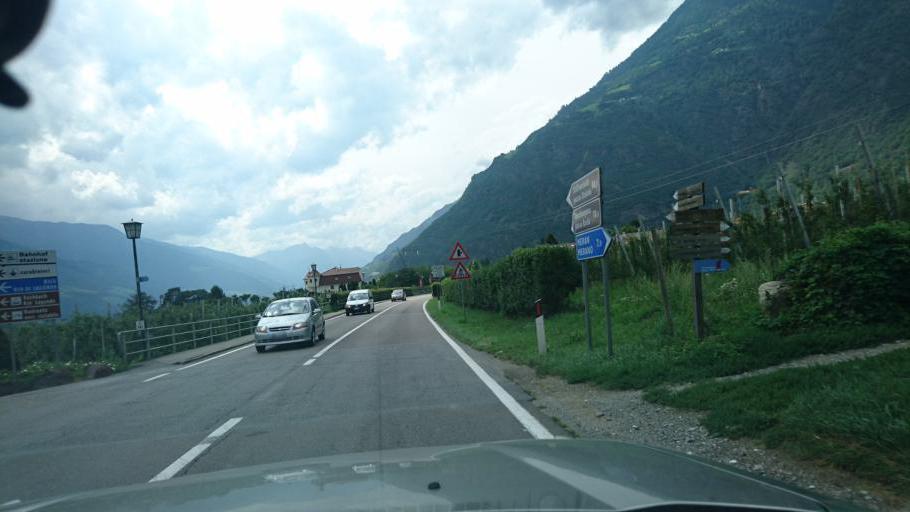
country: IT
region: Trentino-Alto Adige
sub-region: Bolzano
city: Rabla
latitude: 46.6708
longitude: 11.0676
